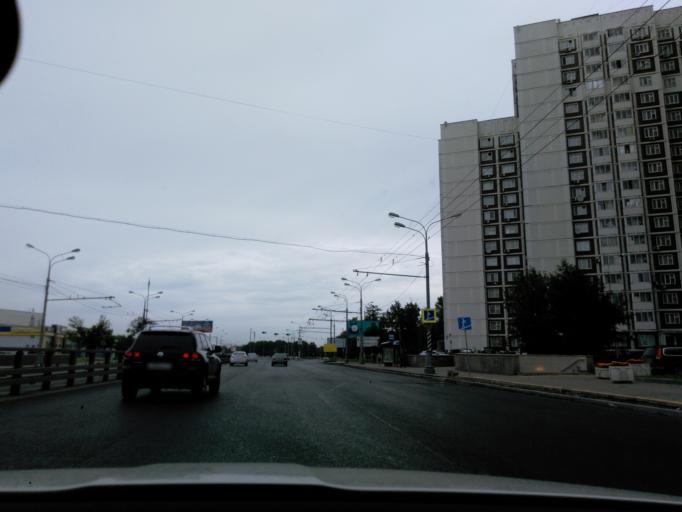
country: RU
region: Moscow
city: Tsaritsyno
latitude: 55.6474
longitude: 37.6569
